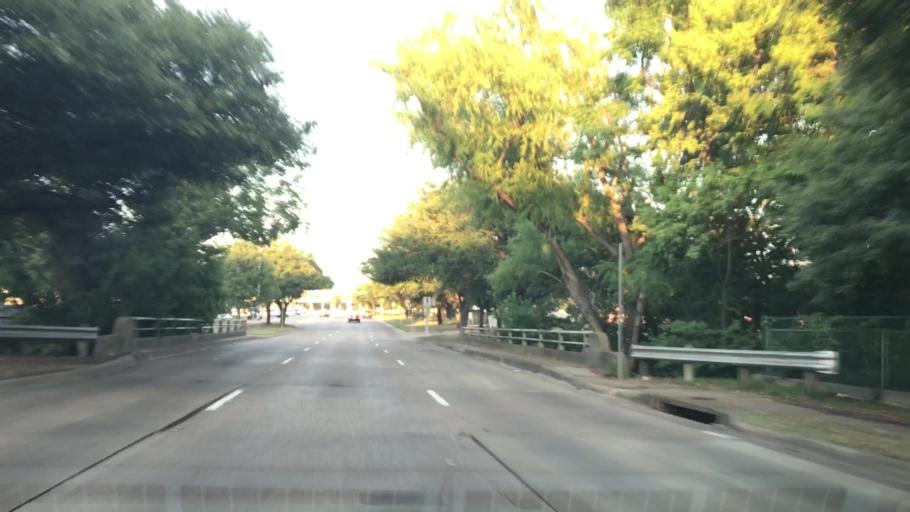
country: US
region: Texas
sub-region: Dallas County
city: Addison
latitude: 32.9095
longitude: -96.8206
